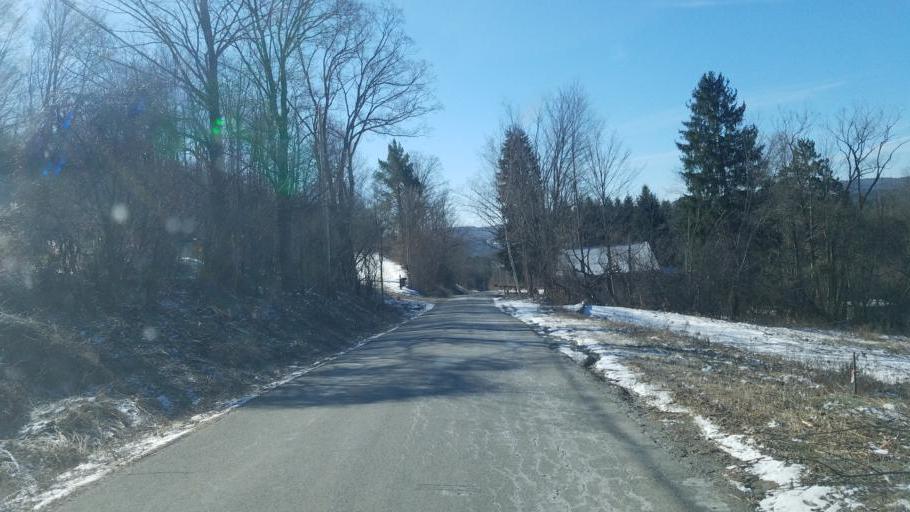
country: US
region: New York
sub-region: Allegany County
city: Wellsville
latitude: 42.1324
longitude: -77.9498
